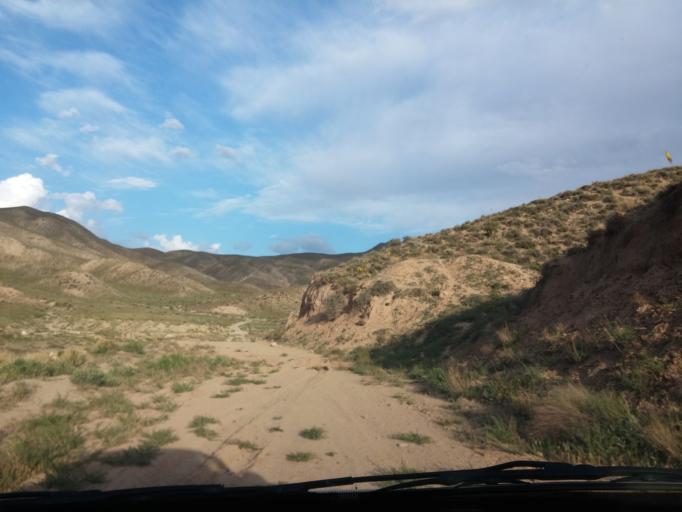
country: IR
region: Semnan
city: Istgah-e Rah Ahan-e Garmsar
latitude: 35.4990
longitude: 52.2868
